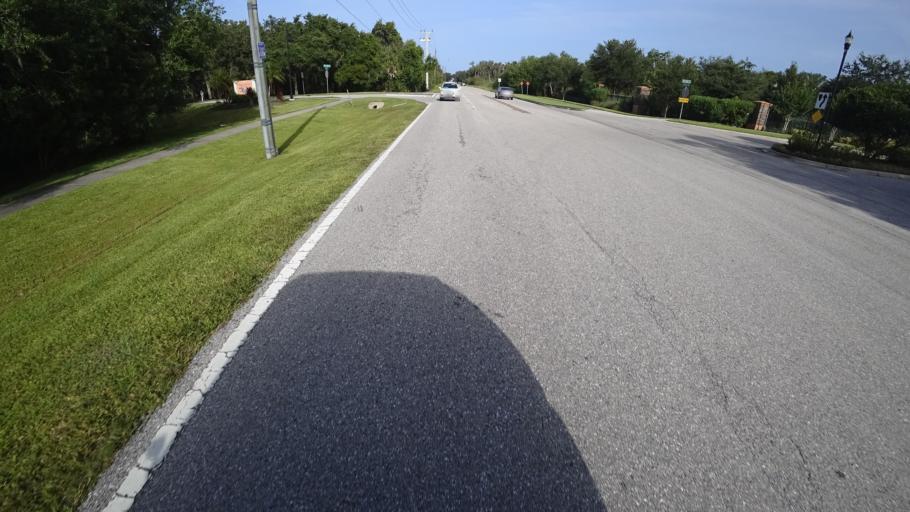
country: US
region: Florida
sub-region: Manatee County
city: Ellenton
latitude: 27.5468
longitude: -82.4929
